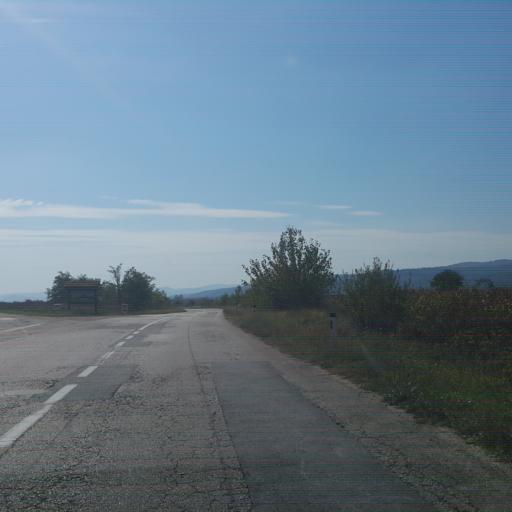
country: RS
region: Central Serbia
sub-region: Zajecarski Okrug
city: Knjazevac
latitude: 43.6612
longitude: 22.2856
